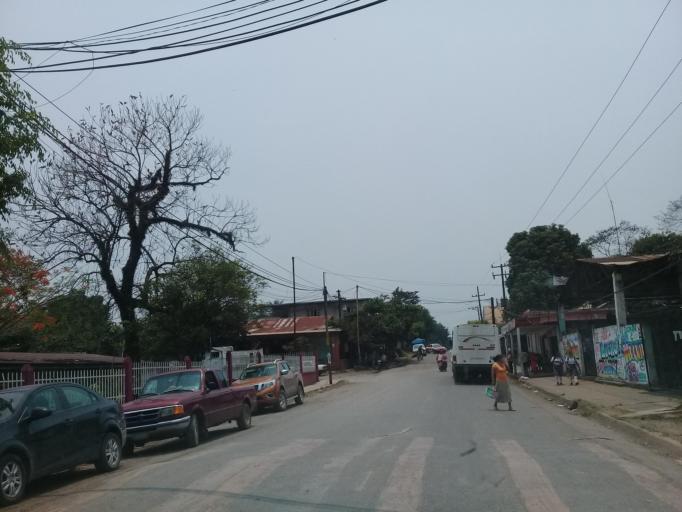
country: MX
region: Veracruz
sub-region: Tezonapa
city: Laguna Chica (Pueblo Nuevo)
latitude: 18.5440
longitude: -96.7350
